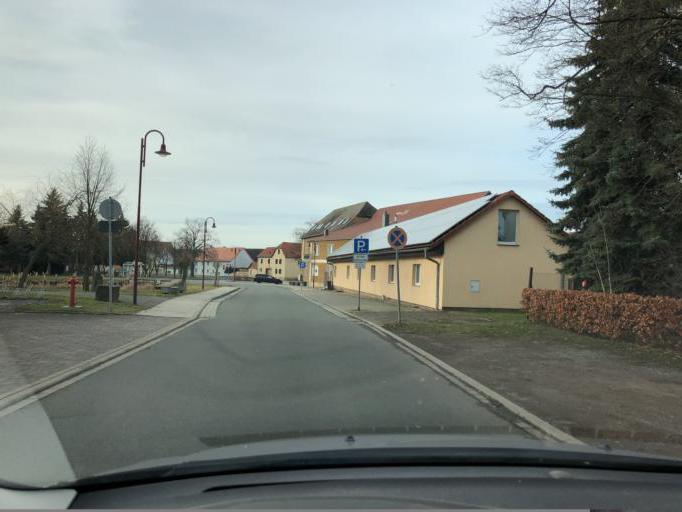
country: DE
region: Thuringia
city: Nirmsdorf
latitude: 51.1444
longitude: 11.4790
